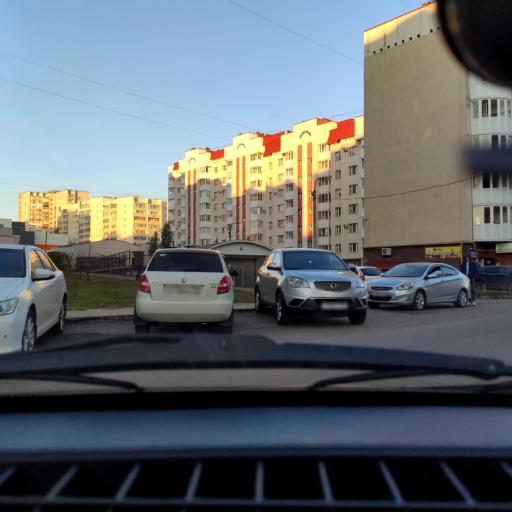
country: RU
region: Bashkortostan
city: Ufa
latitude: 54.6973
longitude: 55.9872
